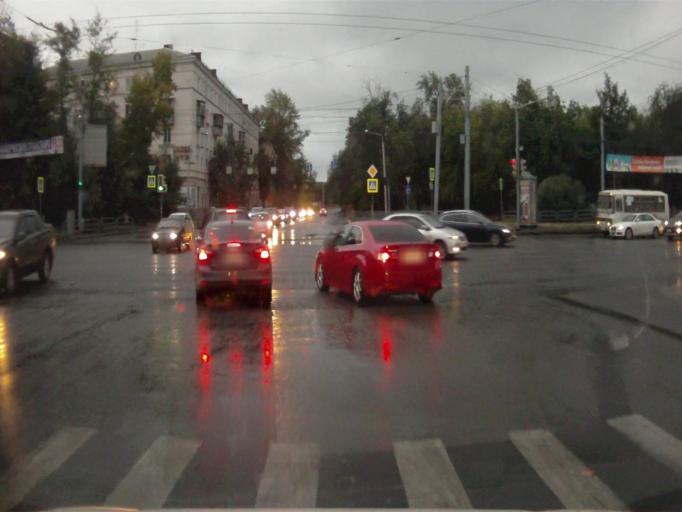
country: RU
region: Chelyabinsk
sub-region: Gorod Chelyabinsk
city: Chelyabinsk
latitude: 55.1615
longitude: 61.4337
